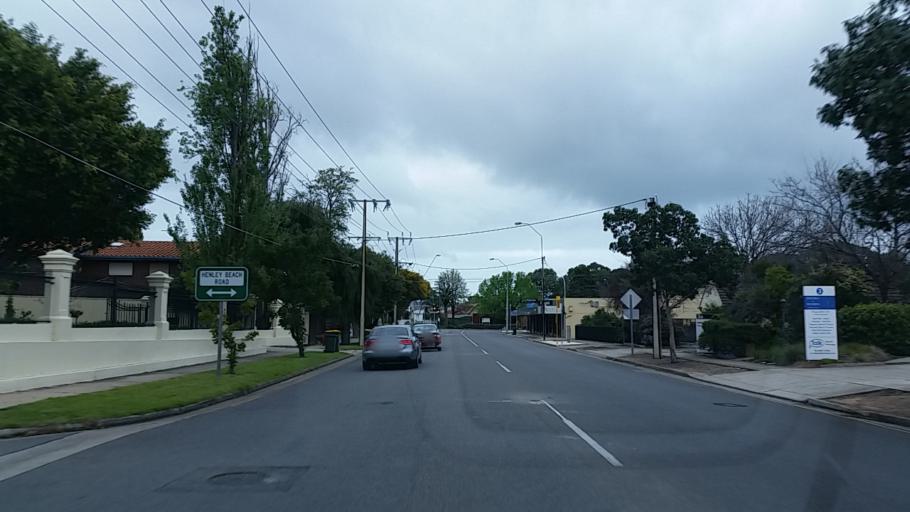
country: AU
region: South Australia
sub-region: Charles Sturt
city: Findon
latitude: -34.9259
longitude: 138.5355
